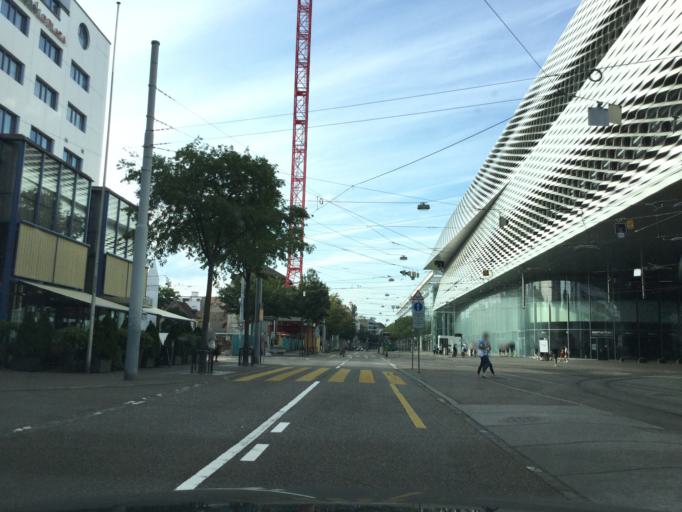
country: CH
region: Basel-Landschaft
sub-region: Bezirk Arlesheim
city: Birsfelden
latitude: 47.5630
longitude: 7.5996
